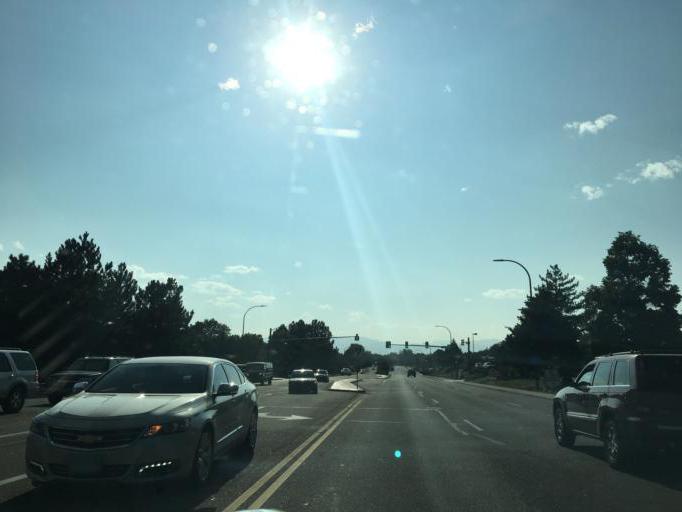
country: US
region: Colorado
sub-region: Adams County
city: Westminster
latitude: 39.8418
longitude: -105.0537
